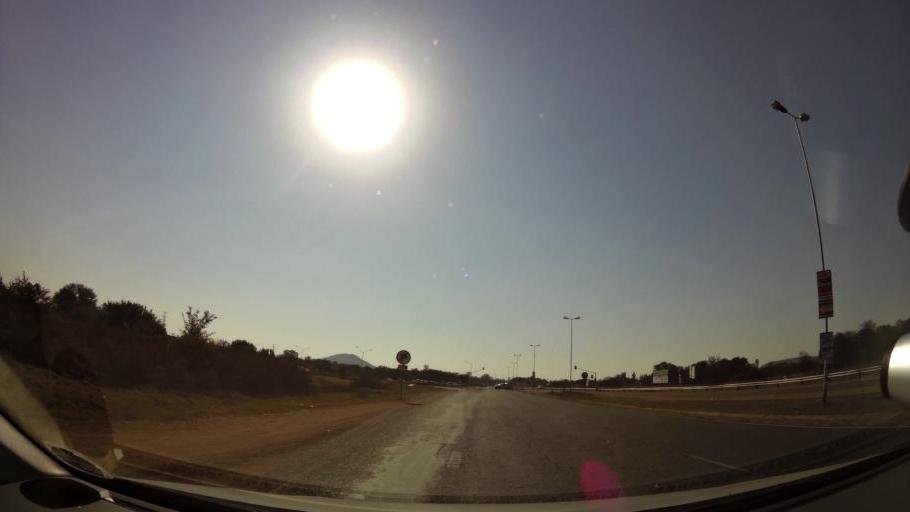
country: ZA
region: Gauteng
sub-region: City of Tshwane Metropolitan Municipality
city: Pretoria
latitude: -25.6621
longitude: 28.1917
